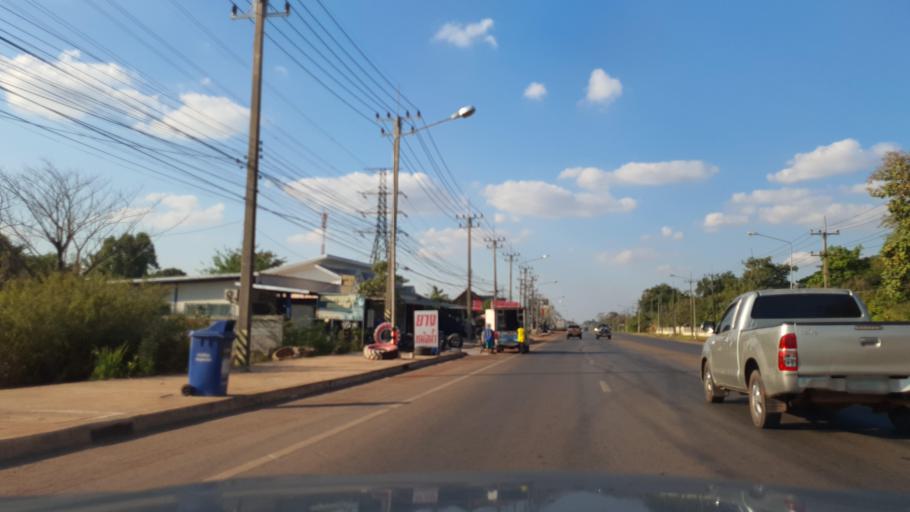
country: TH
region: Sakon Nakhon
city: Sakon Nakhon
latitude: 17.1480
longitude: 104.1079
